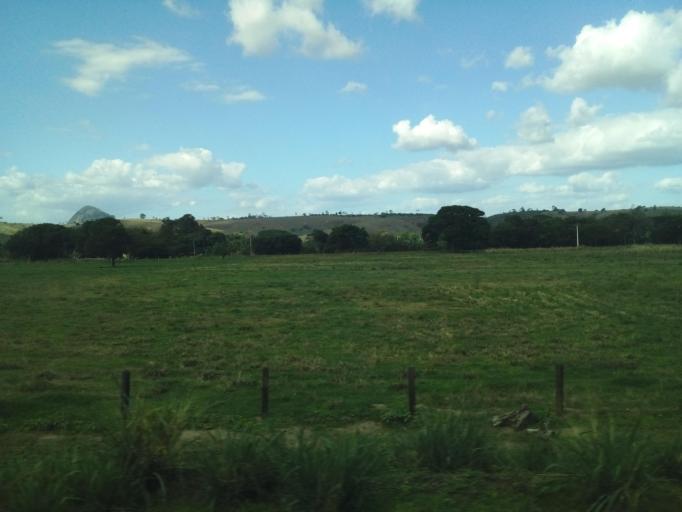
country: BR
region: Minas Gerais
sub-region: Conselheiro Pena
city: Conselheiro Pena
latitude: -18.9959
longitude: -41.5944
